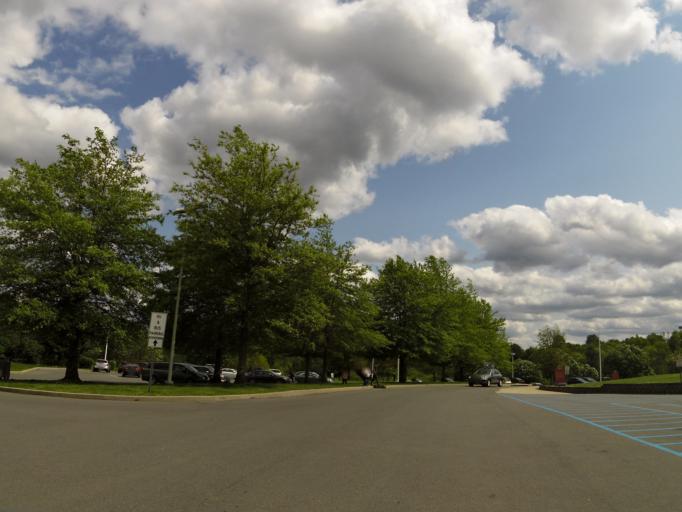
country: US
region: West Virginia
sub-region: Raleigh County
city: Mabscott
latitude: 37.8018
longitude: -81.2165
